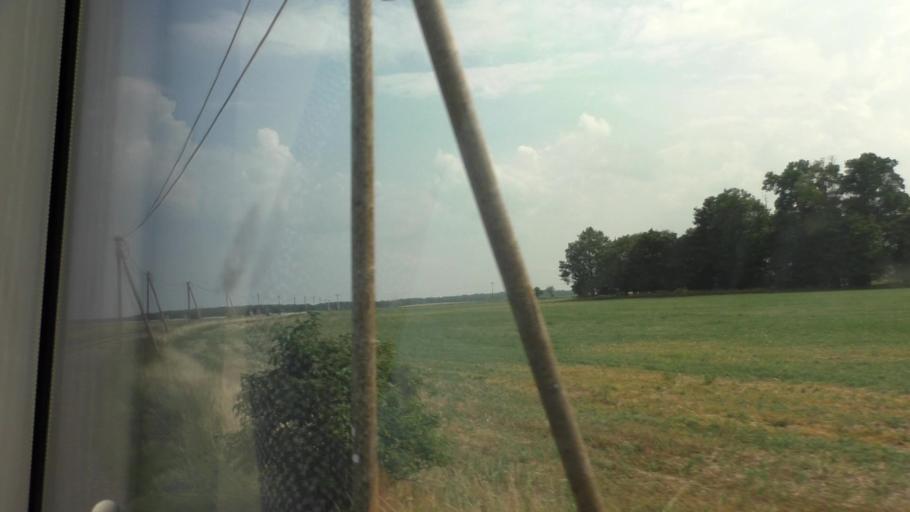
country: DE
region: Brandenburg
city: Rietz Neuendorf
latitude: 52.2034
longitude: 14.1304
